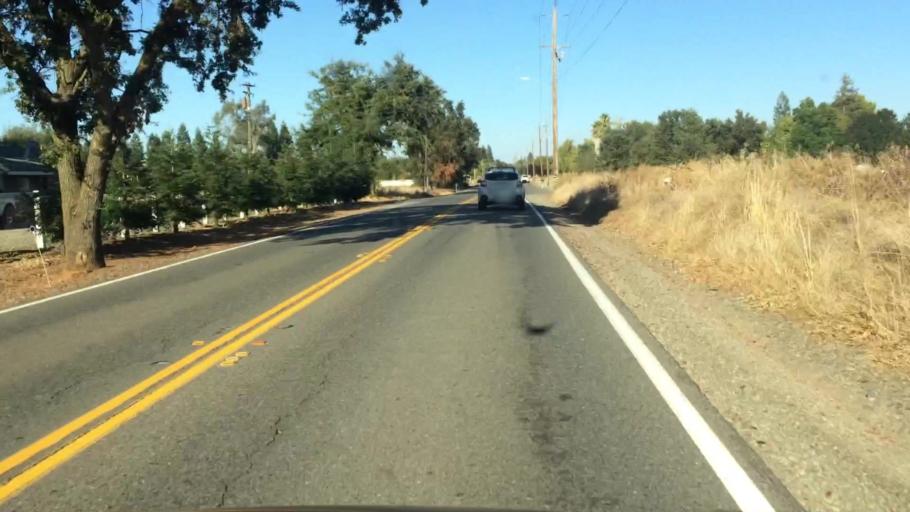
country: US
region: California
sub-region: Sacramento County
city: Wilton
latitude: 38.4335
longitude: -121.1995
